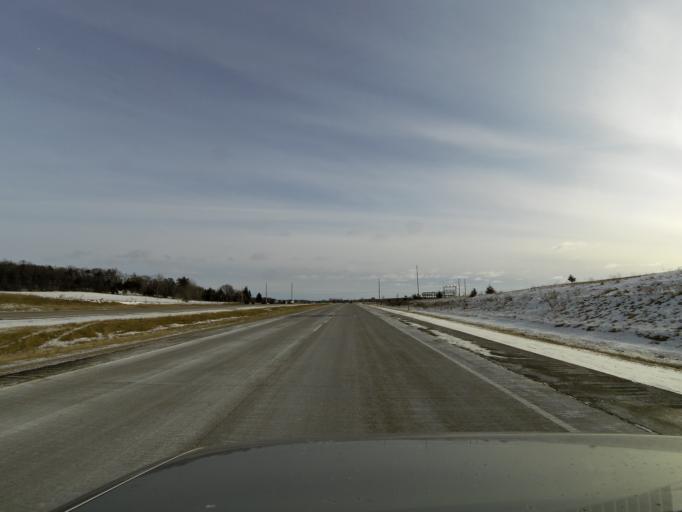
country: US
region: Wisconsin
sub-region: Pierce County
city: River Falls
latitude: 44.9160
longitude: -92.6690
